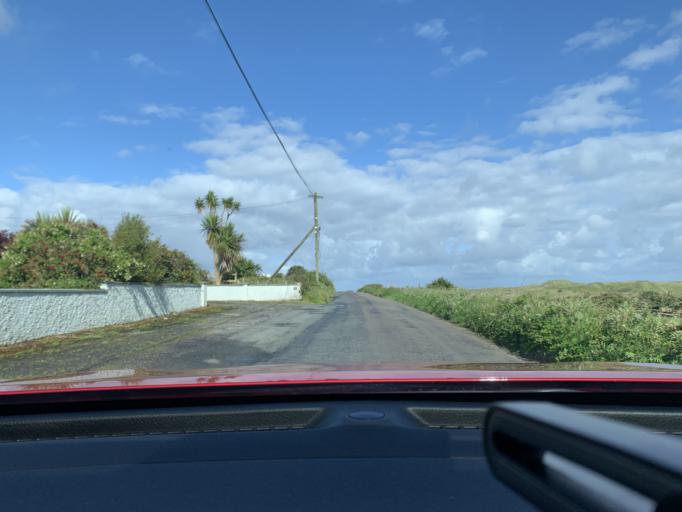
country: IE
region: Connaught
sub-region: Sligo
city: Strandhill
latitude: 54.3958
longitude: -8.5614
